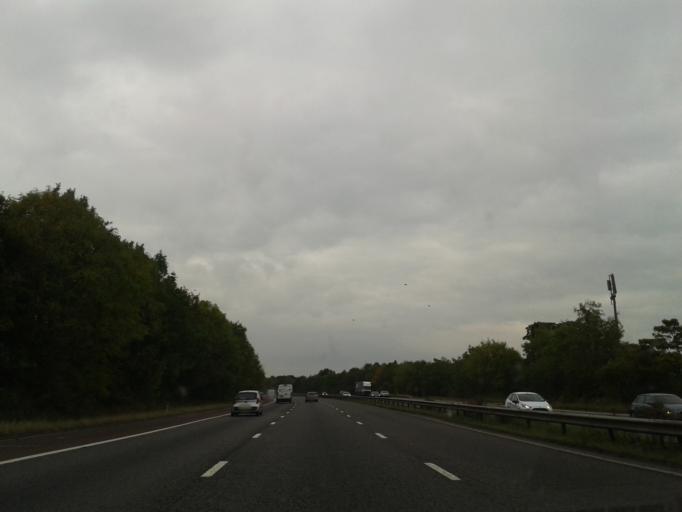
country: GB
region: England
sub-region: Lancashire
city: Garstang
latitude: 53.9299
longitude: -2.7578
